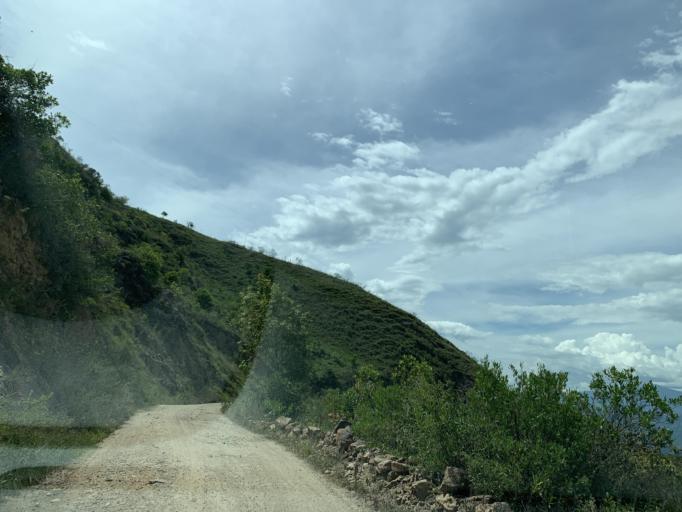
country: CO
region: Boyaca
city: Tipacoque
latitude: 6.4480
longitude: -72.7064
